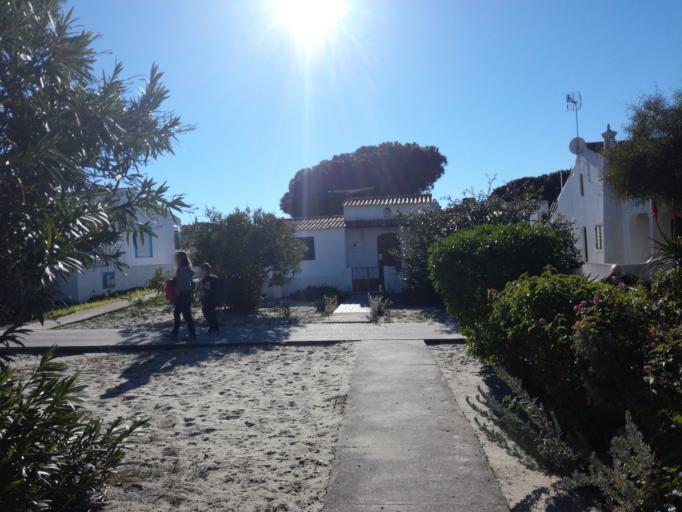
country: PT
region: Faro
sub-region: Olhao
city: Olhao
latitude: 37.0189
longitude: -7.8018
